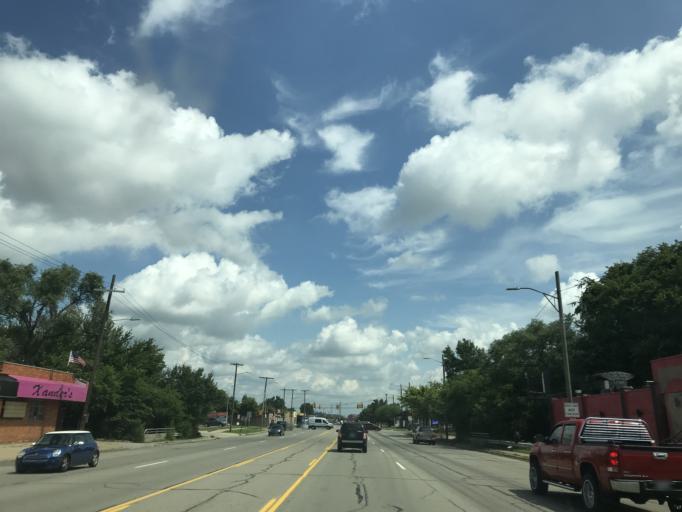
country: US
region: Michigan
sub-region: Wayne County
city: Melvindale
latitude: 42.2687
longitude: -83.1819
